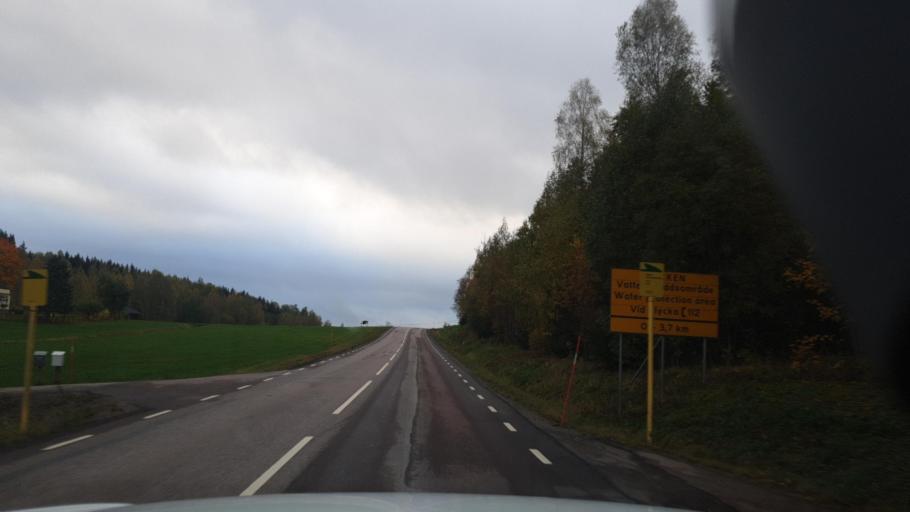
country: SE
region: Vaermland
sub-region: Arvika Kommun
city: Arvika
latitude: 59.7330
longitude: 12.6426
